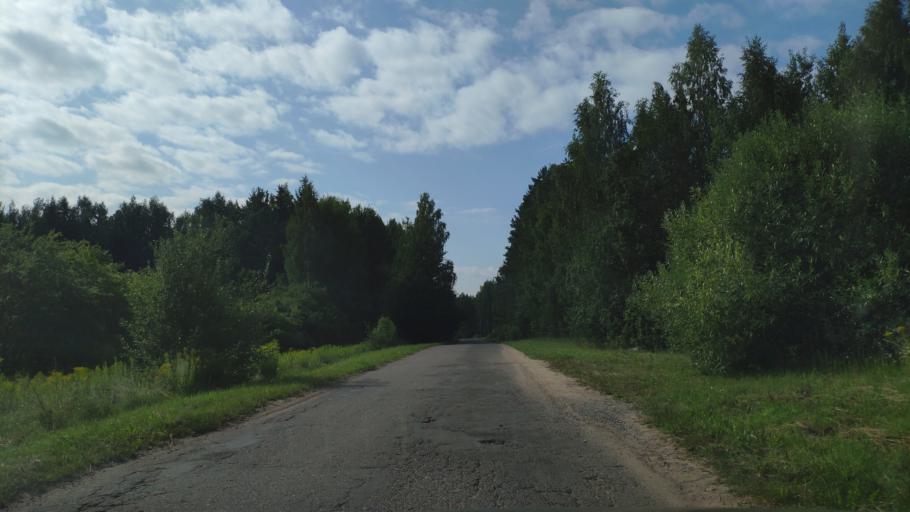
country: BY
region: Minsk
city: Zaslawye
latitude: 53.9836
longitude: 27.2891
